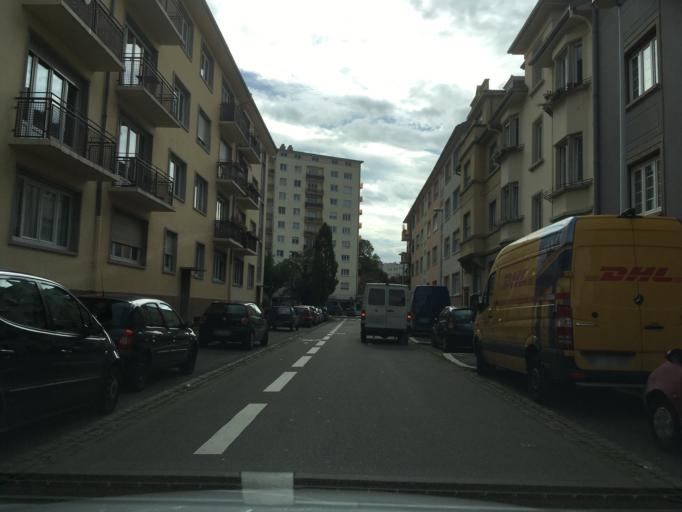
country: FR
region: Alsace
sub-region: Departement du Bas-Rhin
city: Strasbourg
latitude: 48.5664
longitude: 7.7712
